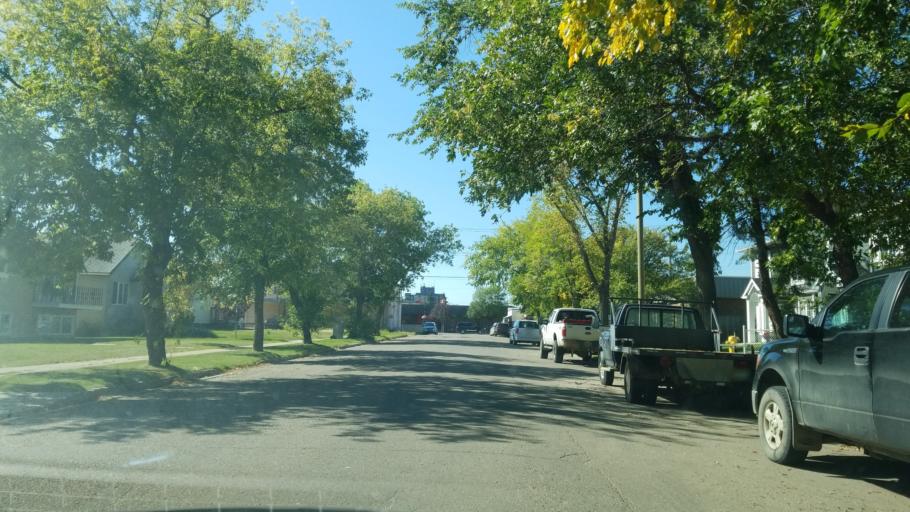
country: CA
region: Saskatchewan
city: Lloydminster
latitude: 53.2807
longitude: -110.0016
